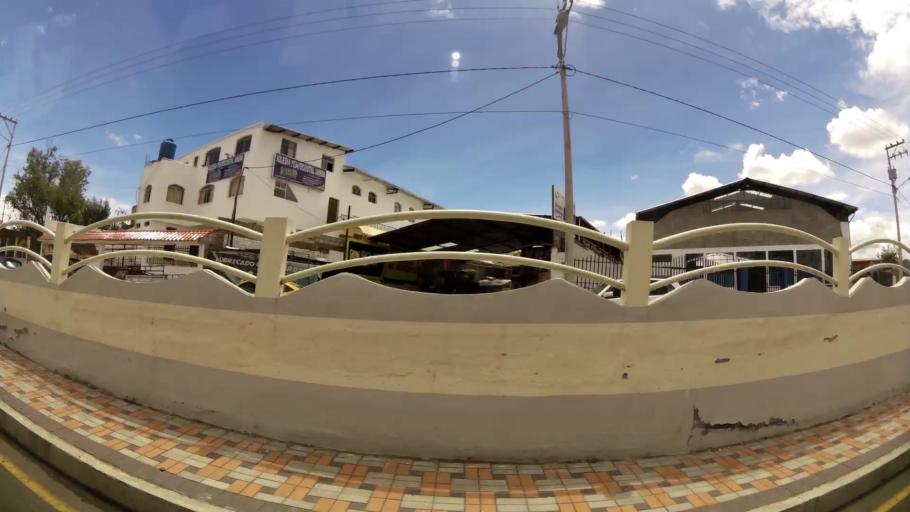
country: EC
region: Tungurahua
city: Ambato
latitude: -1.2587
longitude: -78.6128
